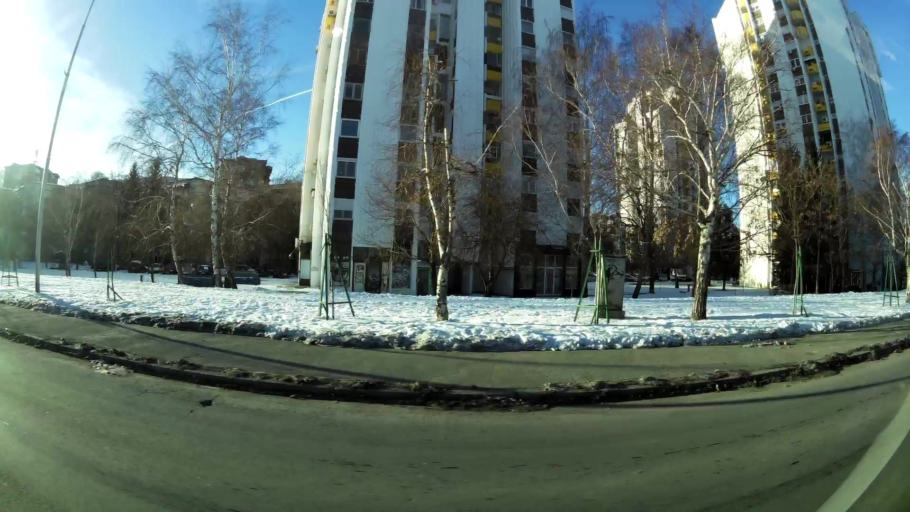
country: MK
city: Krushopek
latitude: 42.0092
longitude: 21.3863
